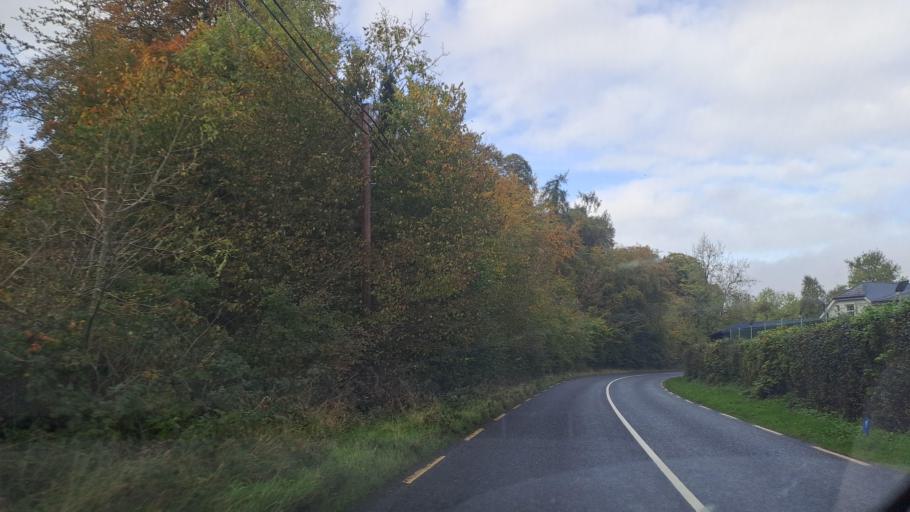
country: IE
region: Ulster
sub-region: County Monaghan
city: Carrickmacross
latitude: 53.9454
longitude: -6.7165
